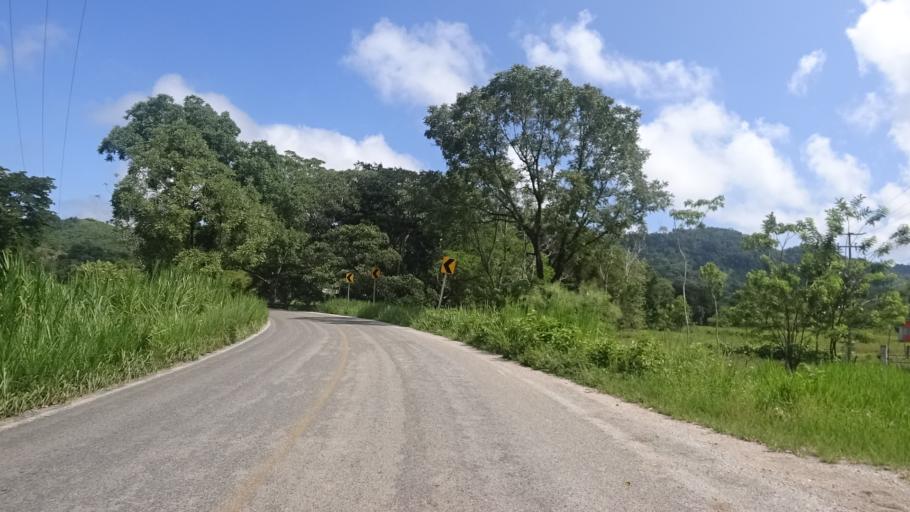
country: MX
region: Chiapas
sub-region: Palenque
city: Doctor Samuel Leon Brindis
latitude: 17.4475
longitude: -91.9614
